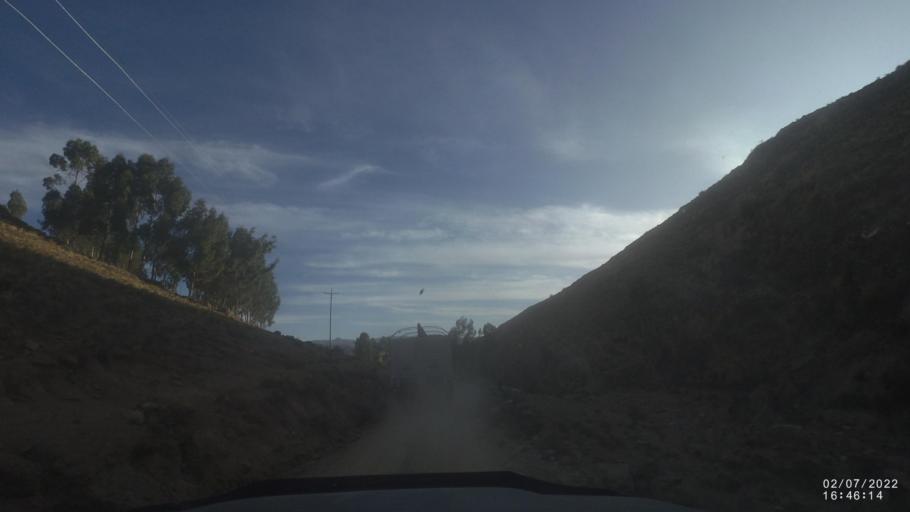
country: BO
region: Cochabamba
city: Irpa Irpa
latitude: -17.9770
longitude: -66.5122
